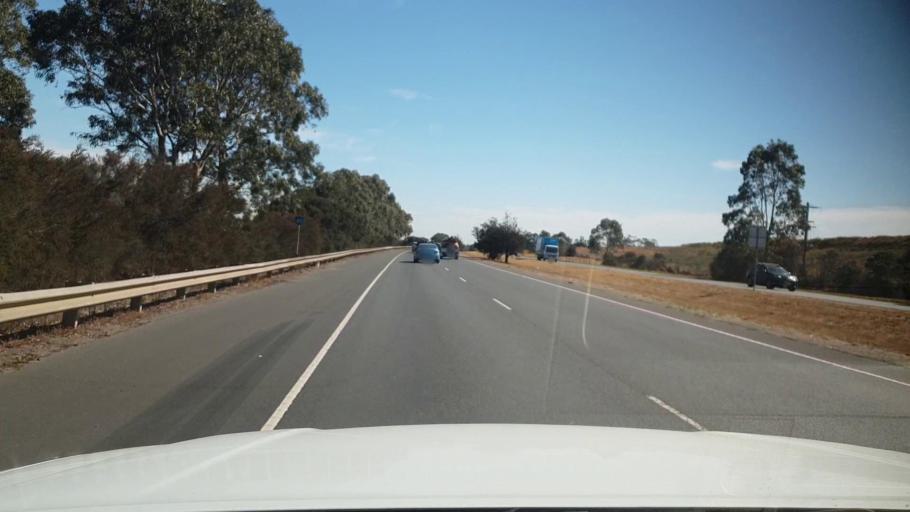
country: AU
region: Victoria
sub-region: Kingston
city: Dingley Village
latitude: -37.9782
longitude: 145.1414
